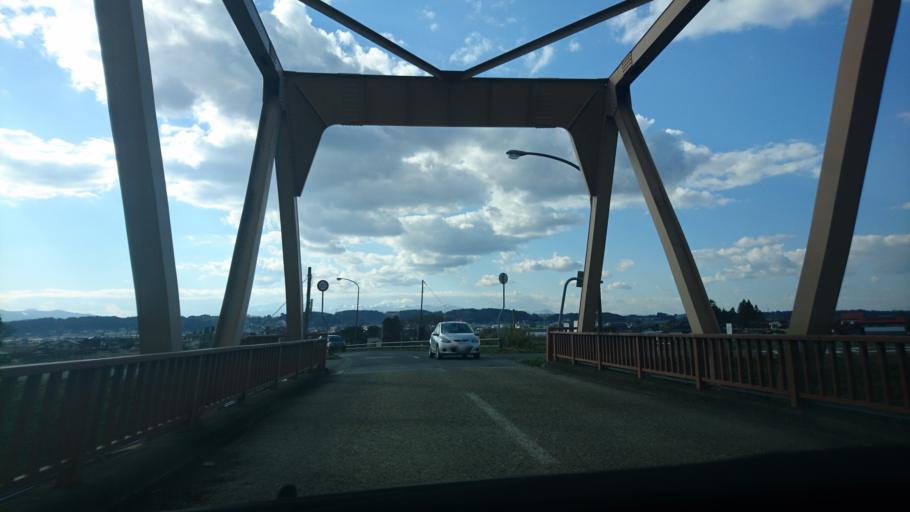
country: JP
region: Iwate
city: Mizusawa
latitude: 39.0420
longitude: 141.1444
